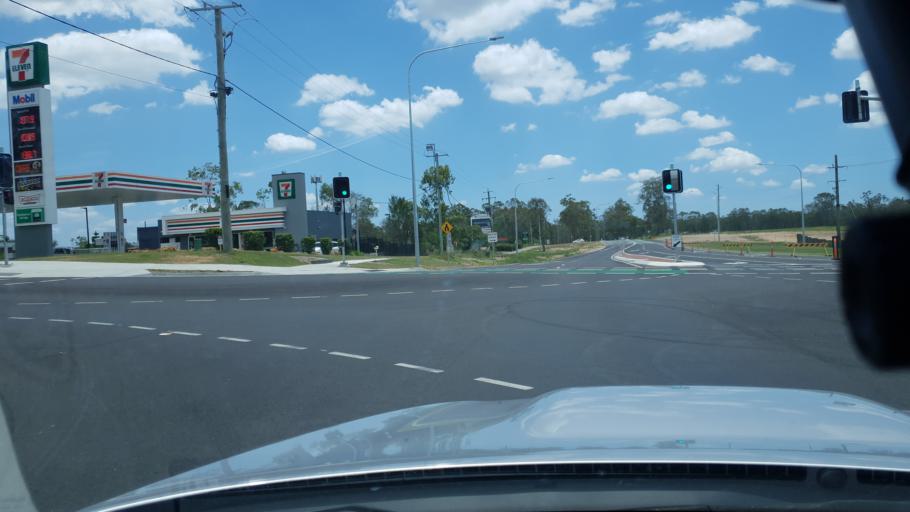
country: AU
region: Queensland
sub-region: Logan
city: North Maclean
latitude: -27.7391
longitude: 152.9845
